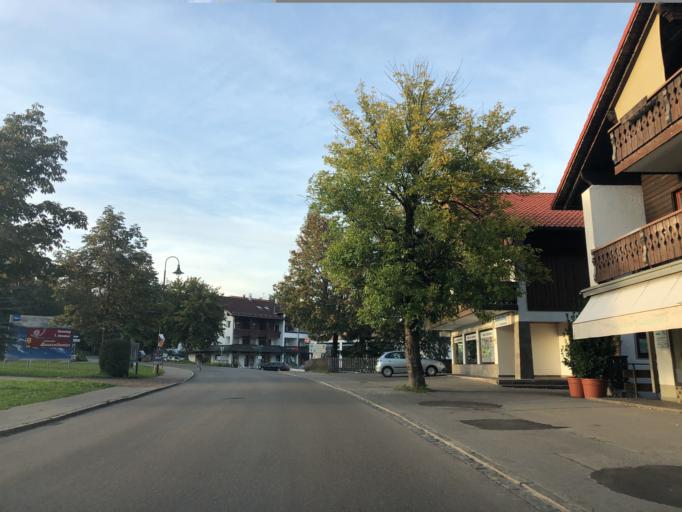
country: DE
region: Bavaria
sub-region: Swabia
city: Pfronten
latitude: 47.5845
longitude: 10.5596
